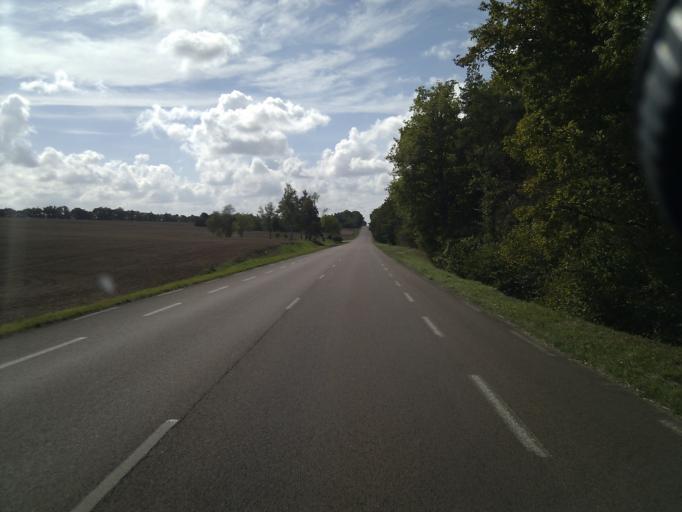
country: FR
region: Bourgogne
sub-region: Departement de la Cote-d'Or
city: Chatillon-sur-Seine
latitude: 47.8273
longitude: 4.5415
